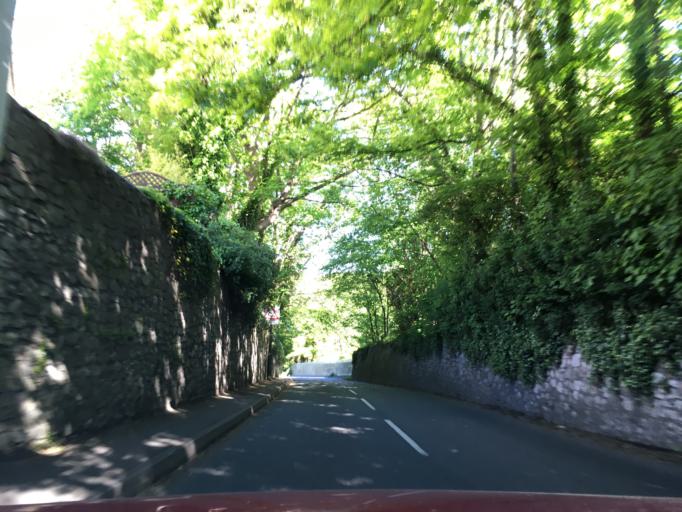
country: GB
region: England
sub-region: South Gloucestershire
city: Severn Beach
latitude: 51.5117
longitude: -2.6386
